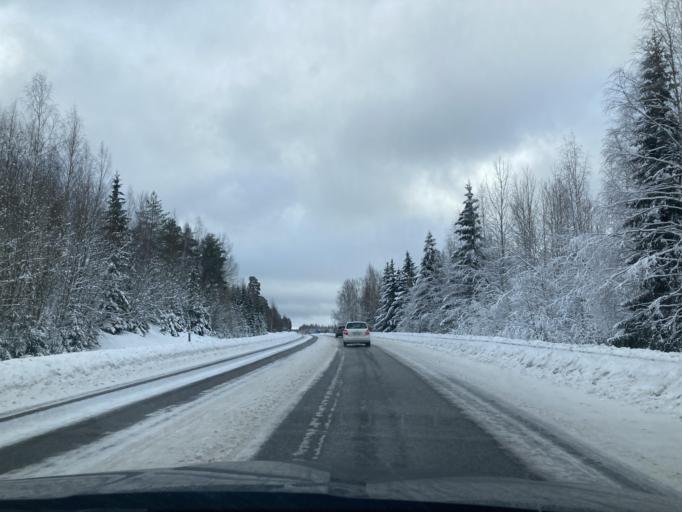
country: FI
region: Central Finland
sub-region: Jaemsae
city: Kuhmoinen
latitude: 61.6671
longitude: 25.2730
